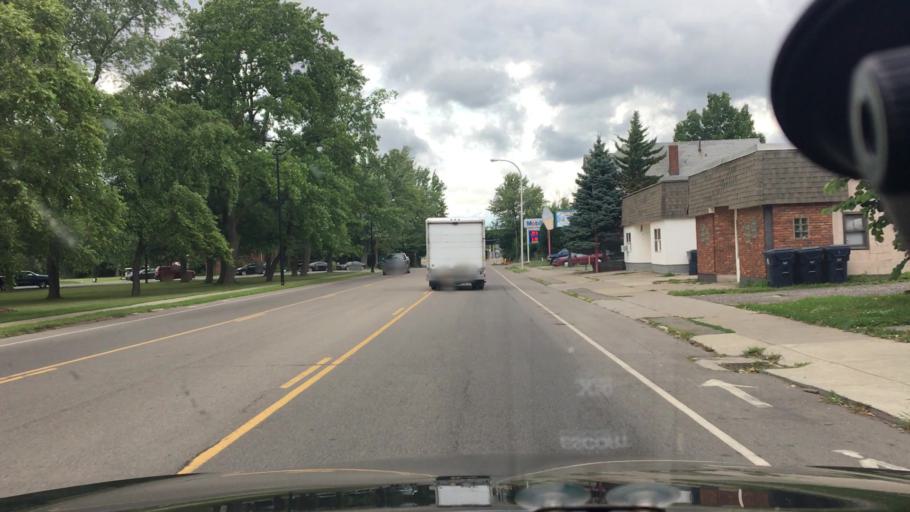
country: US
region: New York
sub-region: Erie County
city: Lackawanna
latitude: 42.8296
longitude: -78.8239
